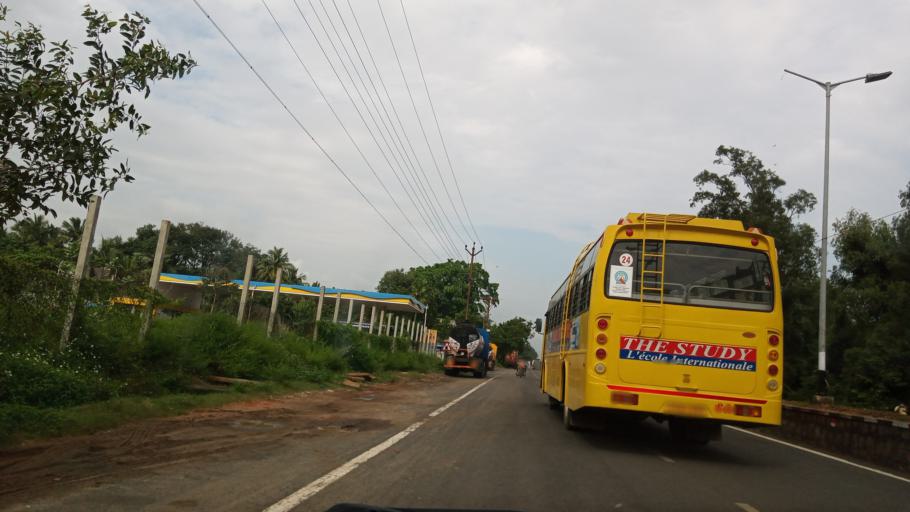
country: IN
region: Tamil Nadu
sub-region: Villupuram
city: Auroville
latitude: 12.0253
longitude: 79.8616
